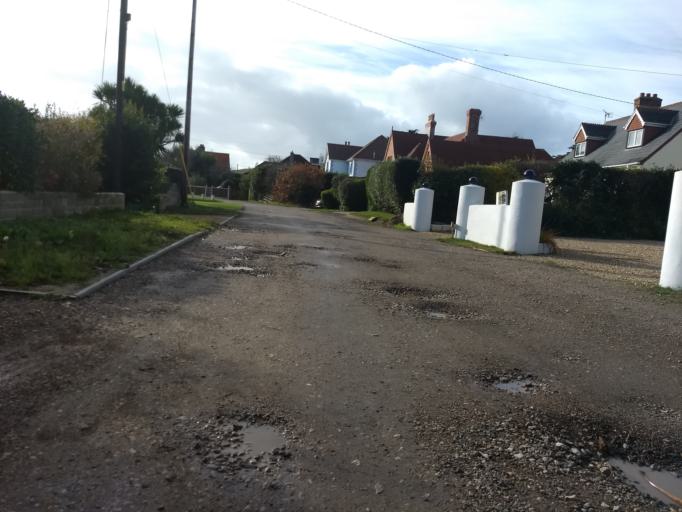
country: GB
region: England
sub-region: Isle of Wight
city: Freshwater
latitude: 50.6728
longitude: -1.5123
